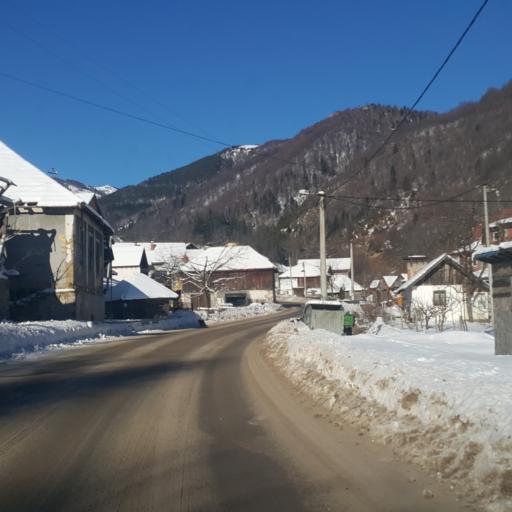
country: XK
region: Mitrovica
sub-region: Komuna e Leposaviqit
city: Leposaviq
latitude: 43.3016
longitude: 20.8824
